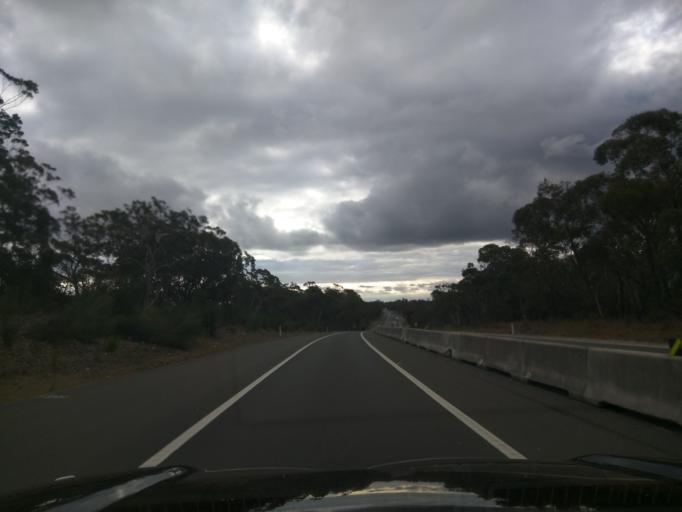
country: AU
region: New South Wales
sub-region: Wollongong
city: Mount Keira
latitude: -34.3320
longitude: 150.7788
